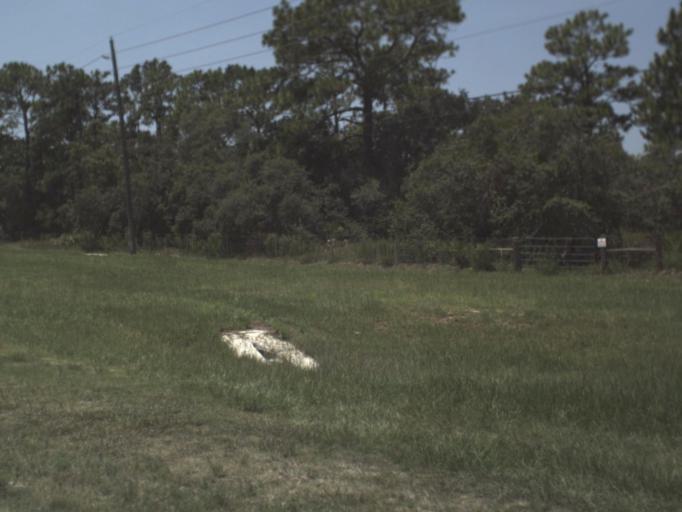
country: US
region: Florida
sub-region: Hernando County
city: North Weeki Wachee
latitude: 28.5545
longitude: -82.5623
